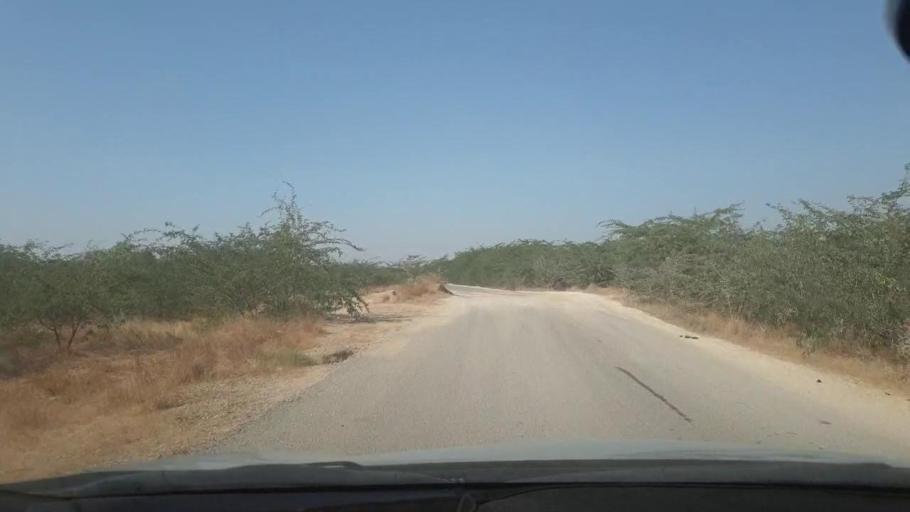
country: PK
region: Sindh
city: Malir Cantonment
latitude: 25.1468
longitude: 67.1663
